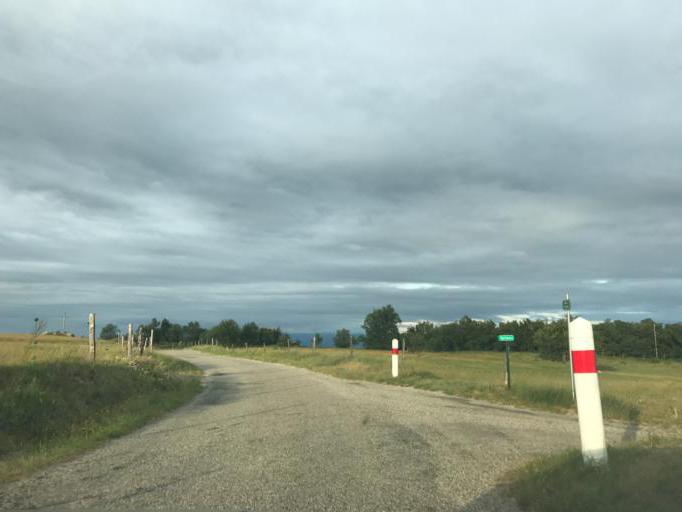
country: FR
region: Rhone-Alpes
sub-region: Departement de l'Ardeche
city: Saint-Julien-en-Saint-Alban
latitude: 44.7967
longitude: 4.7155
